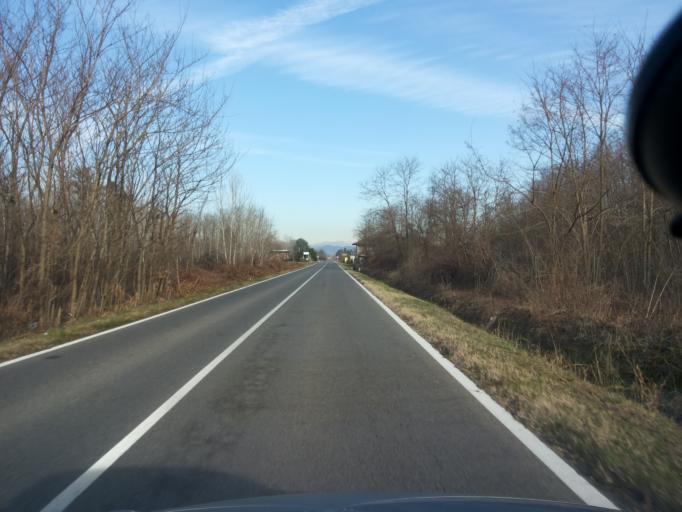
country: IT
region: Piedmont
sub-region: Provincia di Vercelli
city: Arborio
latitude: 45.5121
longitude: 8.3878
